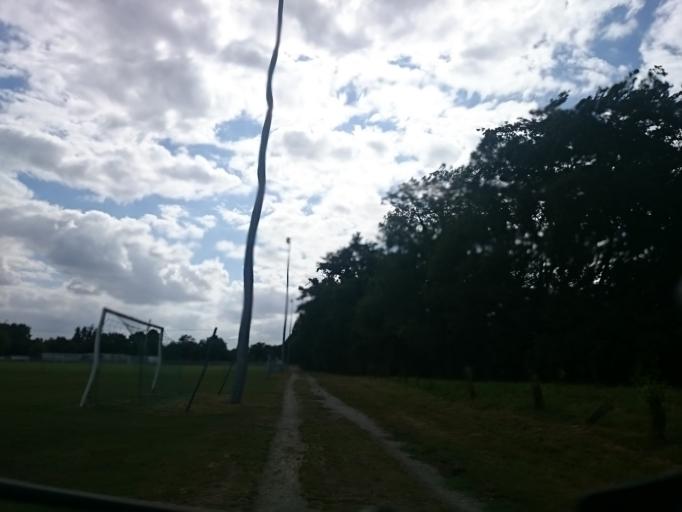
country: FR
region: Brittany
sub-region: Departement d'Ille-et-Vilaine
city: Cesson-Sevigne
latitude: 48.1270
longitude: -1.5870
